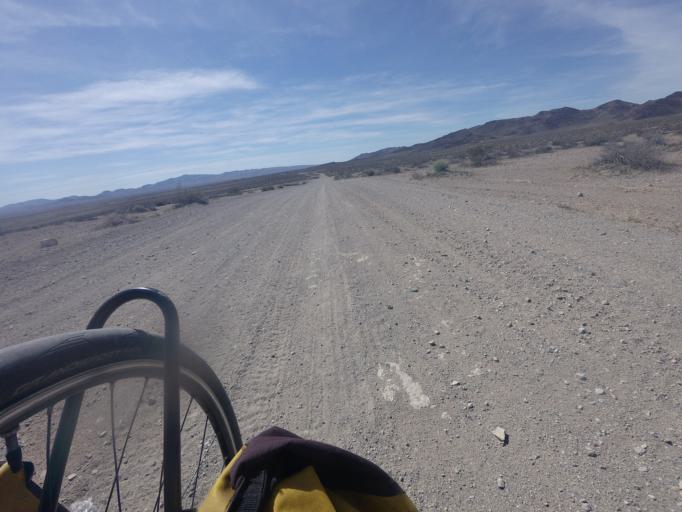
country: US
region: California
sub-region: San Bernardino County
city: Searles Valley
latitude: 35.5905
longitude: -117.4162
